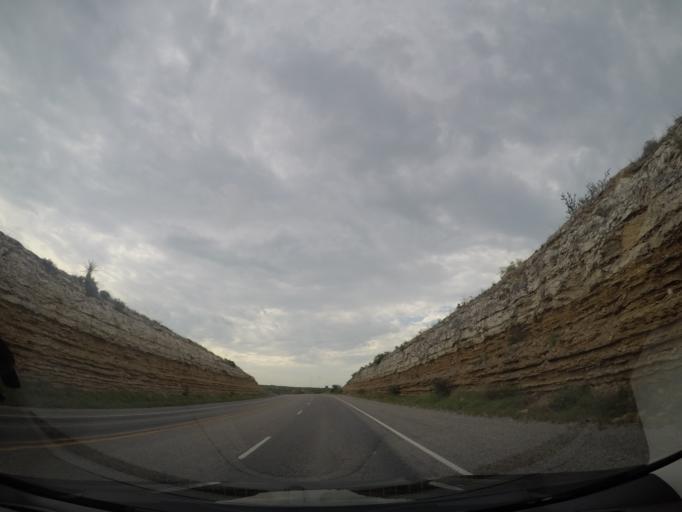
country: US
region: Texas
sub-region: Val Verde County
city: Cienegas Terrace
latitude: 29.7046
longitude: -101.3471
